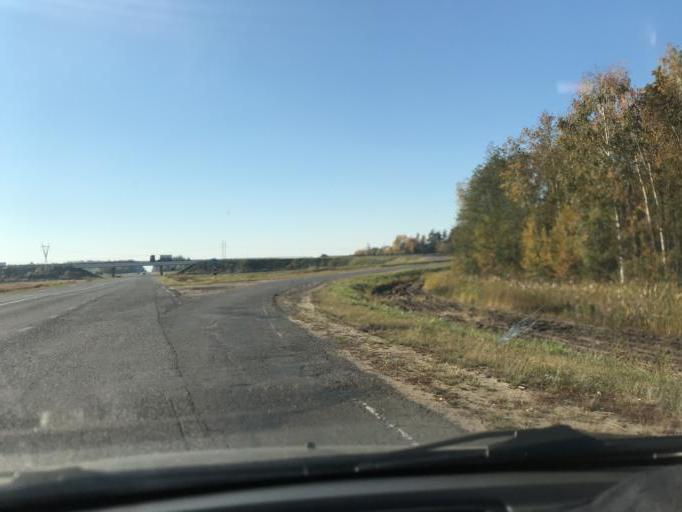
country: BY
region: Mogilev
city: Babruysk
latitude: 53.1065
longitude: 29.0616
